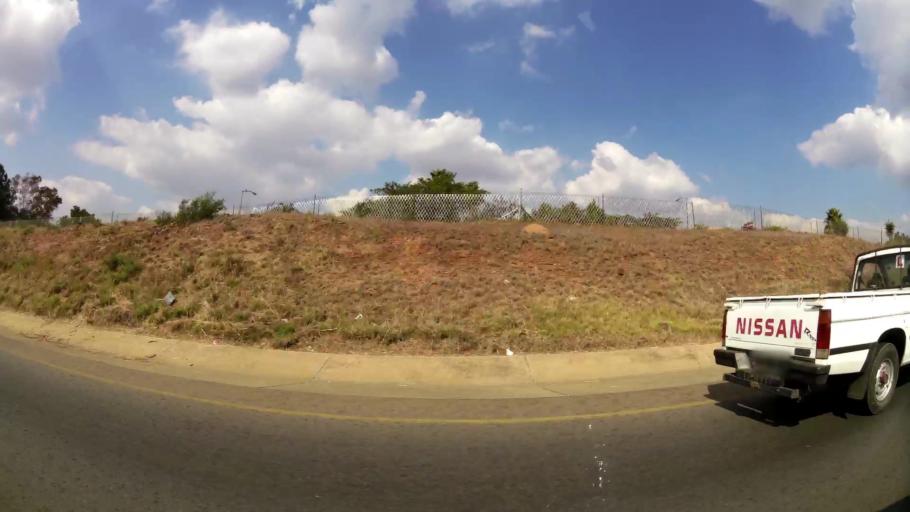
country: ZA
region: Gauteng
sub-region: City of Tshwane Metropolitan Municipality
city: Centurion
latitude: -25.8128
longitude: 28.2801
